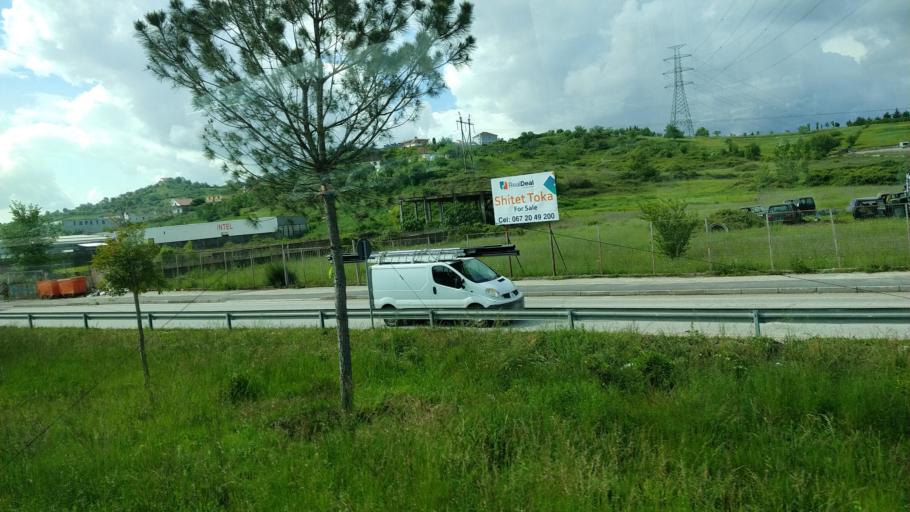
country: AL
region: Tirane
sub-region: Rrethi i Tiranes
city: Kashar
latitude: 41.3649
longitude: 19.7090
